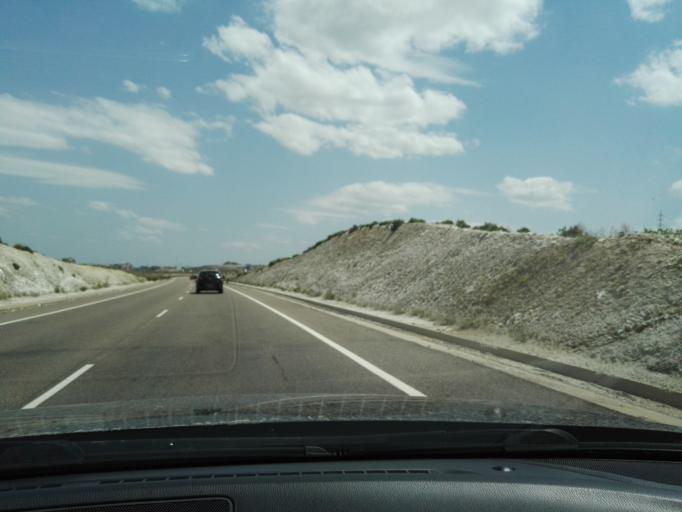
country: ES
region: Aragon
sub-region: Provincia de Zaragoza
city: Montecanal
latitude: 41.6216
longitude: -0.9777
